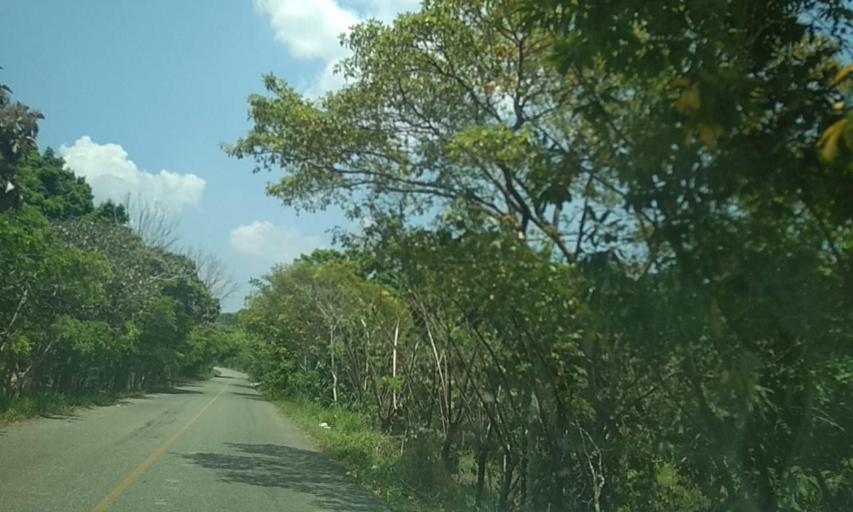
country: MX
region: Tabasco
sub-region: Huimanguillo
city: Francisco Rueda
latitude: 17.8362
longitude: -93.9142
